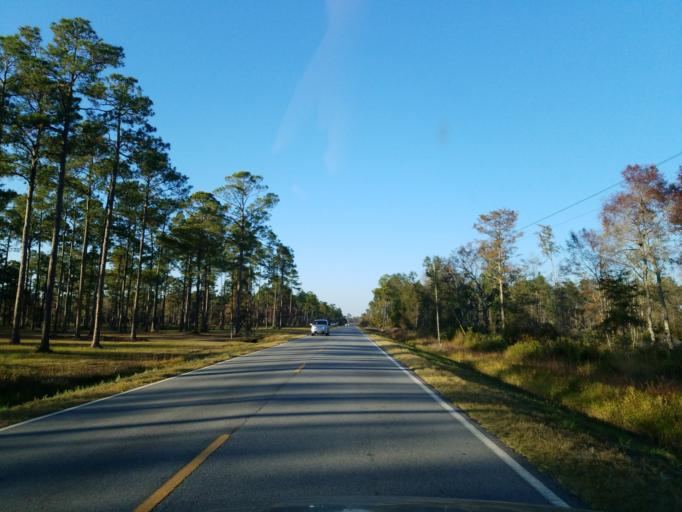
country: US
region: Georgia
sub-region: Lanier County
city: Lakeland
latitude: 31.1199
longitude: -83.0834
